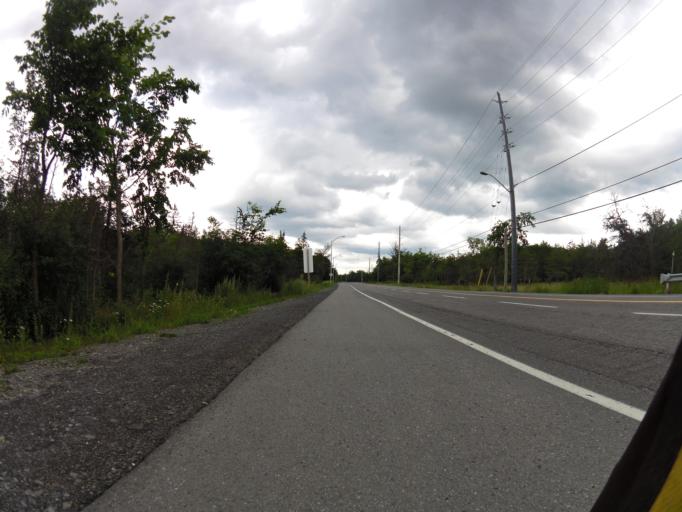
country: CA
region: Ontario
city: Bells Corners
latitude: 45.3024
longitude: -75.8294
